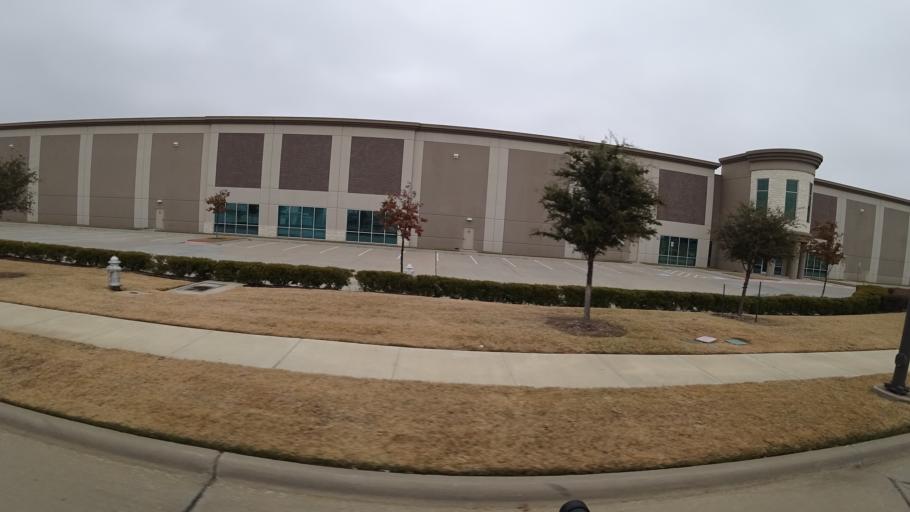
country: US
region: Texas
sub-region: Denton County
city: The Colony
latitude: 33.0608
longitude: -96.9051
